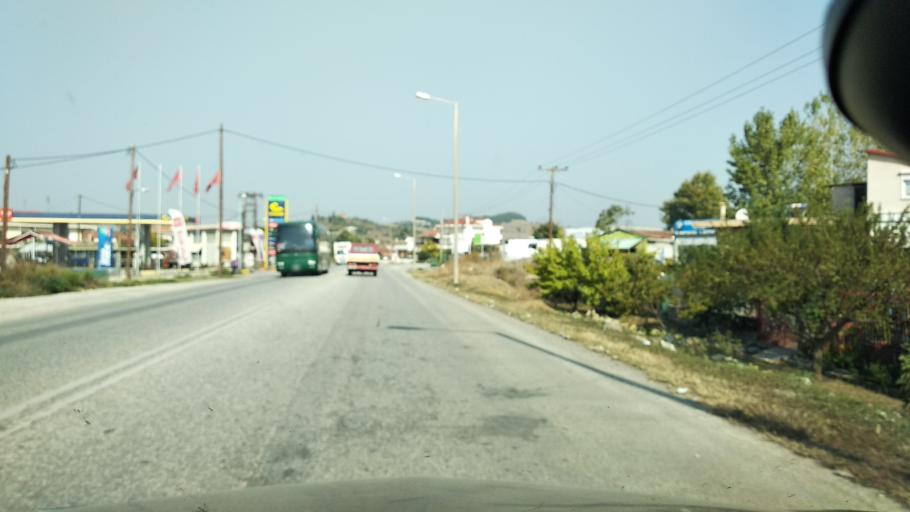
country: GR
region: Thessaly
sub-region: Trikala
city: Trikala
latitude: 39.5622
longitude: 21.7817
